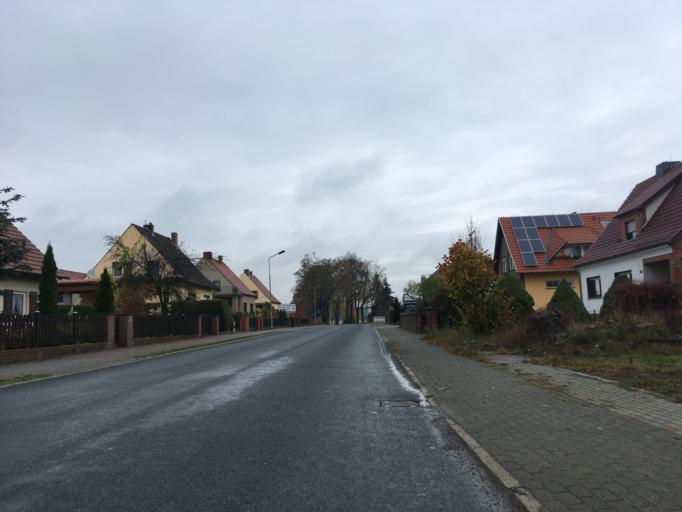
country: DE
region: Brandenburg
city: Neu Zauche
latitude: 52.0202
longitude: 14.1746
